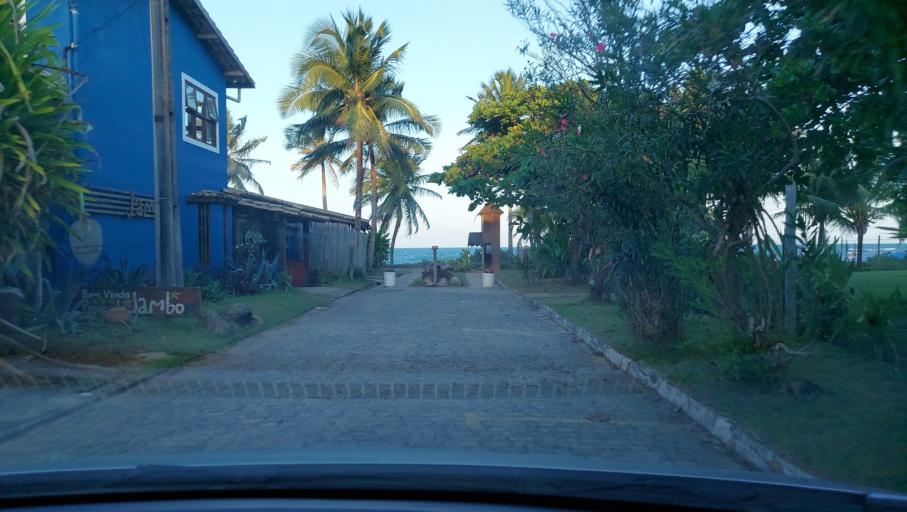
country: BR
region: Bahia
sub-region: Mata De Sao Joao
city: Mata de Sao Joao
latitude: -12.6270
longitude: -38.0462
